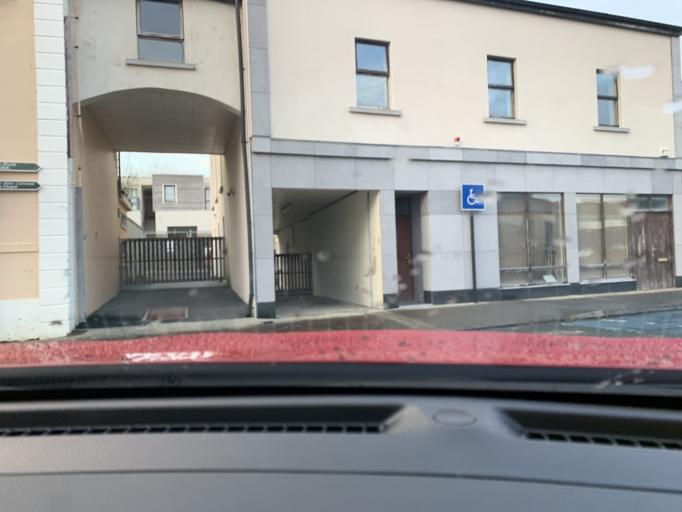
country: IE
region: Connaught
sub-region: County Leitrim
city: Carrick-on-Shannon
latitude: 53.9450
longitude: -8.0964
